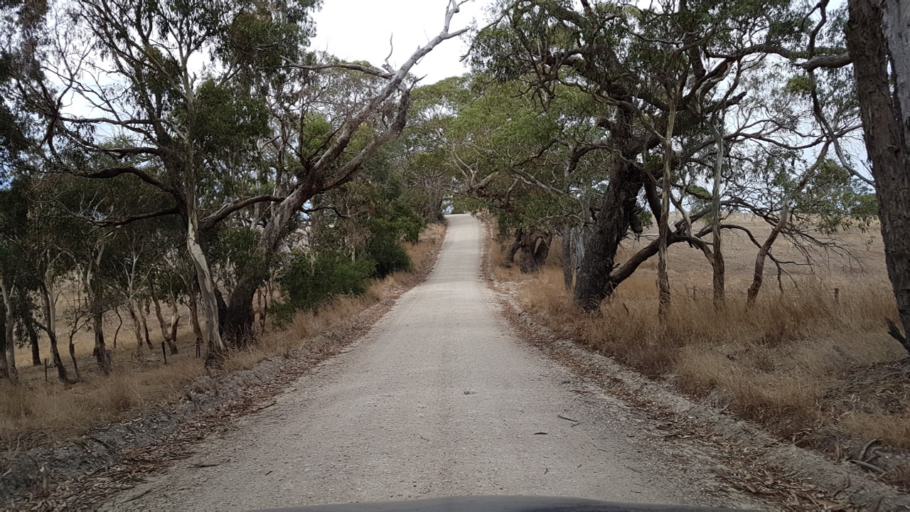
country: AU
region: South Australia
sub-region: Adelaide Hills
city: Birdwood
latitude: -34.7615
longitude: 138.9946
